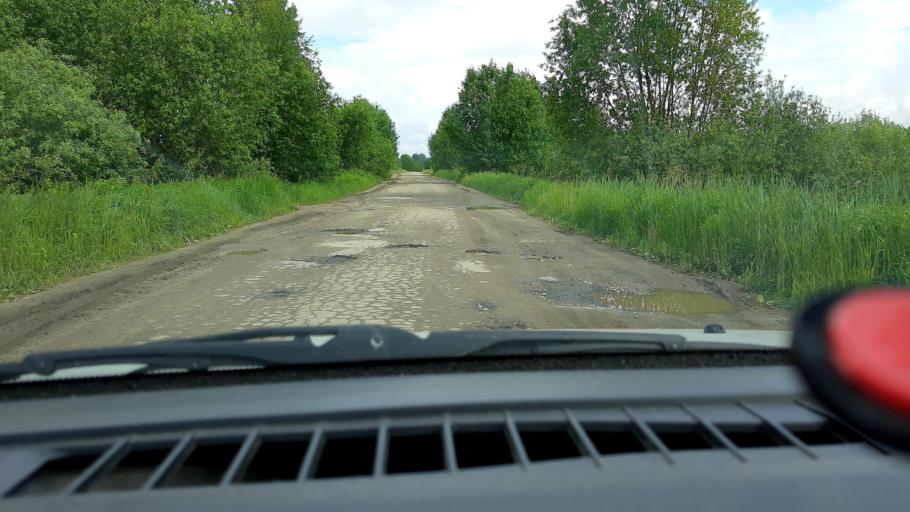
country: RU
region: Nizjnij Novgorod
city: Neklyudovo
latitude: 56.4293
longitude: 43.9623
